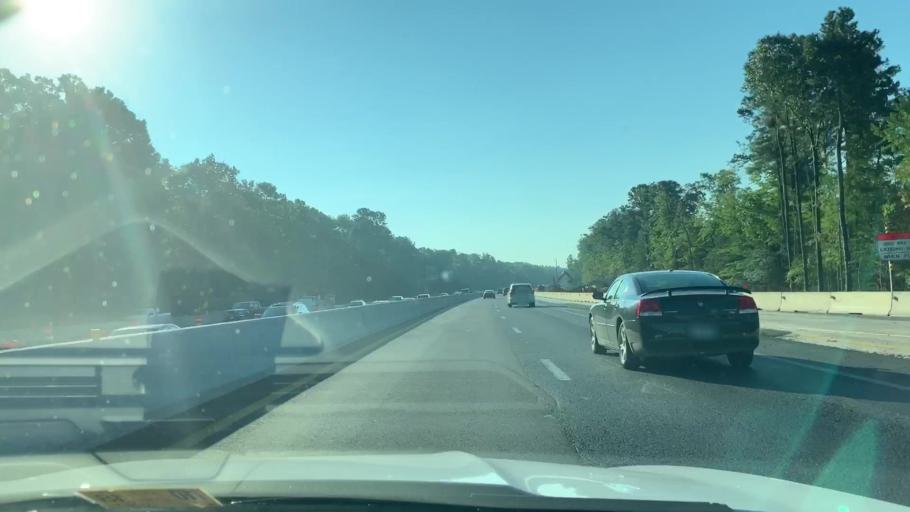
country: US
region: Virginia
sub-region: York County
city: Yorktown
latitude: 37.2033
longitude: -76.5724
